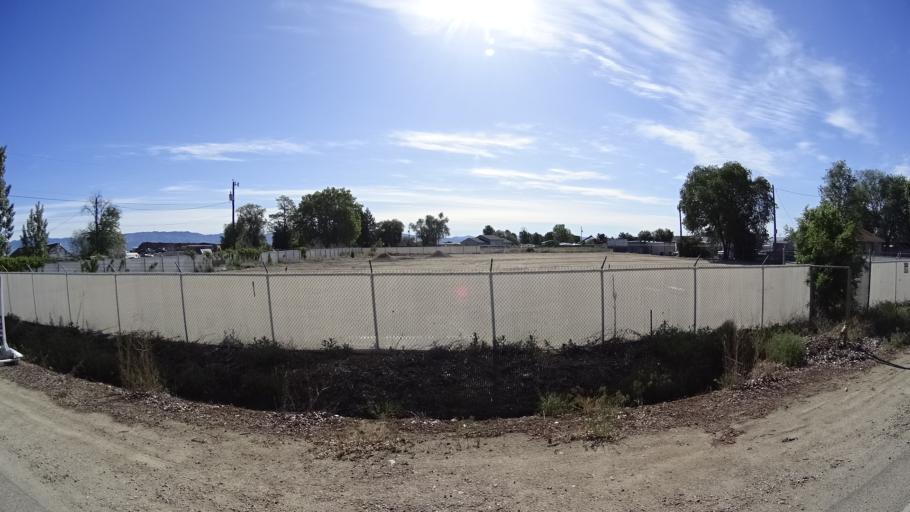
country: US
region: Idaho
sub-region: Ada County
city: Garden City
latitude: 43.5630
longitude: -116.2595
